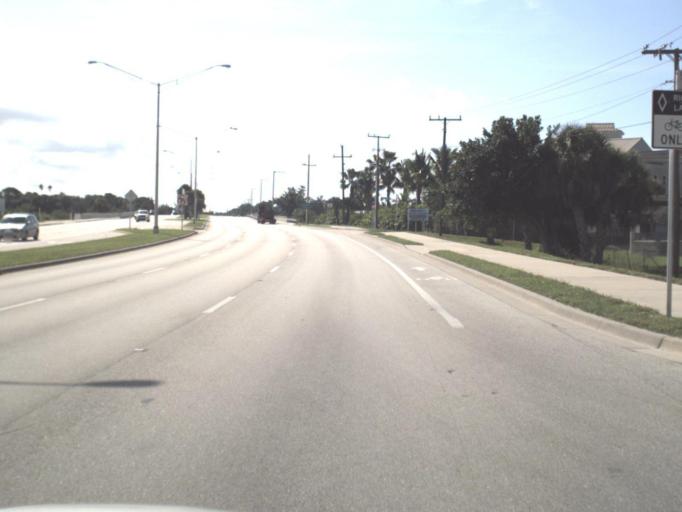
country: US
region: Florida
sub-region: Sarasota County
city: Nokomis
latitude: 27.1214
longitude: -82.4533
